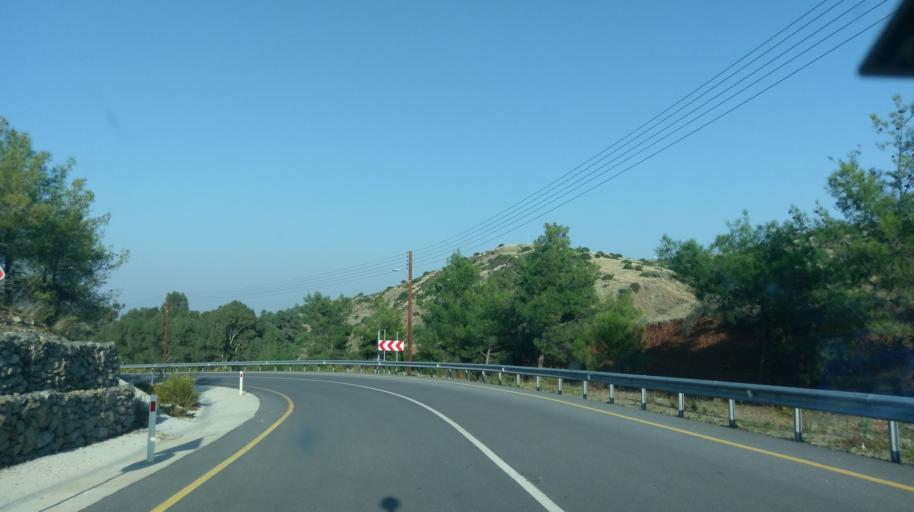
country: CY
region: Lefkosia
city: Lefka
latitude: 35.0834
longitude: 32.8405
